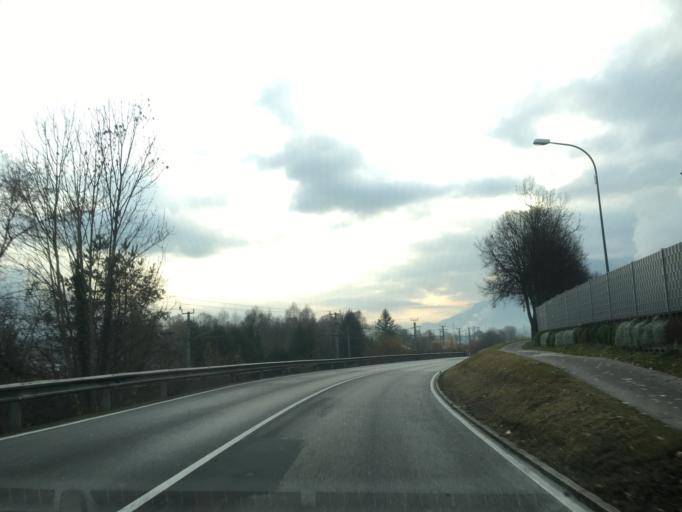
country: AT
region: Vorarlberg
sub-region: Politischer Bezirk Feldkirch
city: Gofis
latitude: 47.2231
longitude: 9.6322
